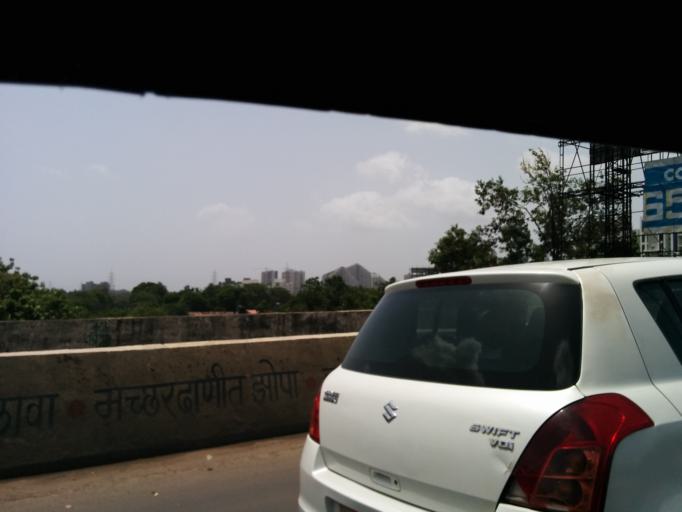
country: IN
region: Maharashtra
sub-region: Pune Division
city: Lohogaon
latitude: 18.5265
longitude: 73.9322
